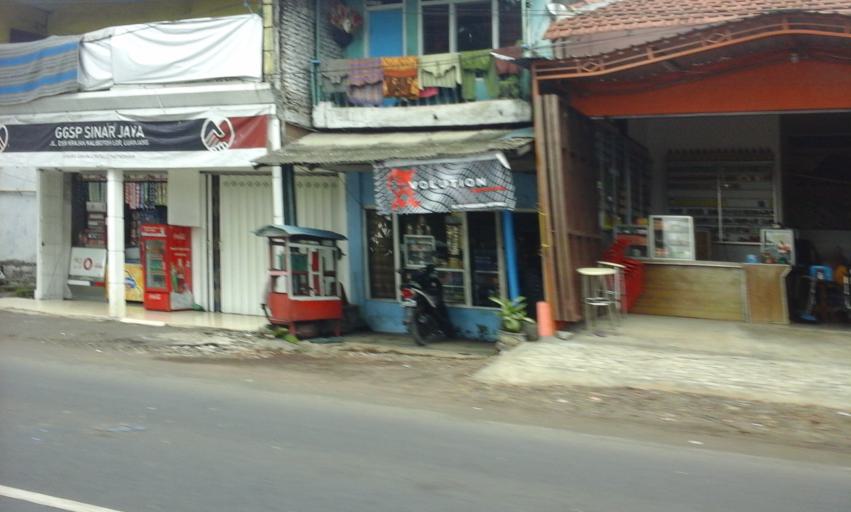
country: ID
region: East Java
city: Jatiroto
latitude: -8.1195
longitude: 113.3586
